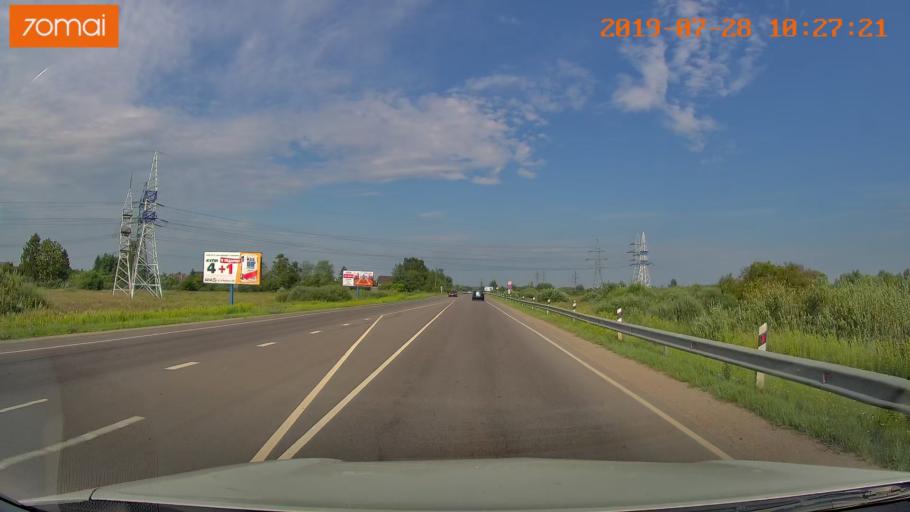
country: RU
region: Kaliningrad
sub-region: Gorod Kaliningrad
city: Kaliningrad
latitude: 54.7704
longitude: 20.5191
